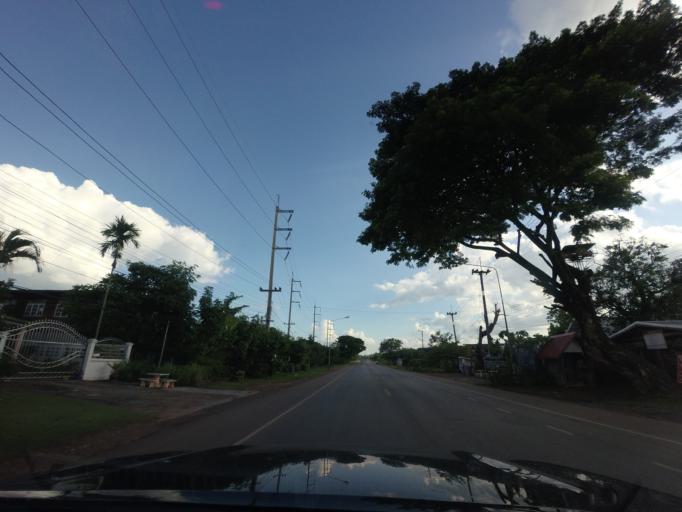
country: TH
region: Changwat Udon Thani
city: Thung Fon
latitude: 17.5069
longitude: 103.2035
